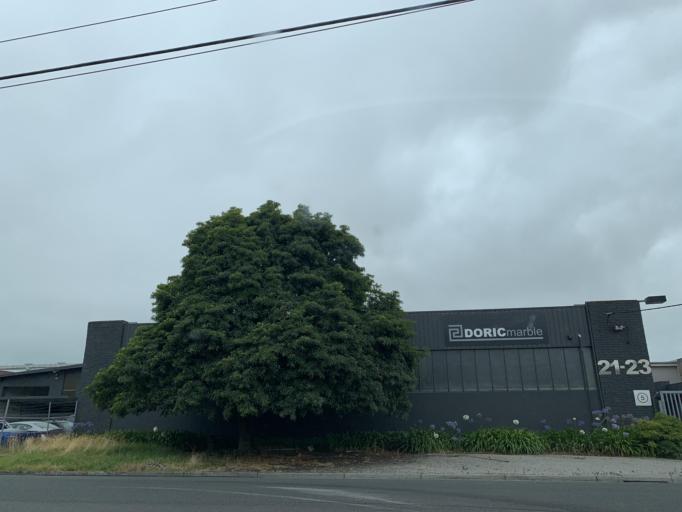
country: AU
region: Victoria
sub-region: Kingston
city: Dingley Village
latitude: -37.9893
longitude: 145.1114
